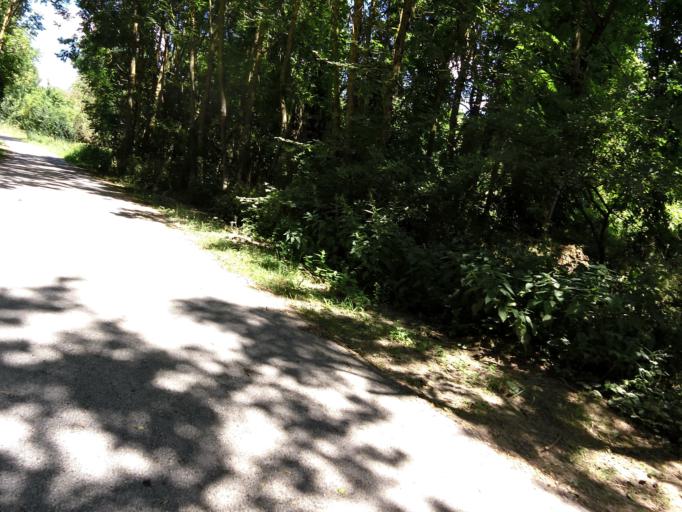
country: DE
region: Bavaria
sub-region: Regierungsbezirk Unterfranken
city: Wuerzburg
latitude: 49.8203
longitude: 9.9536
